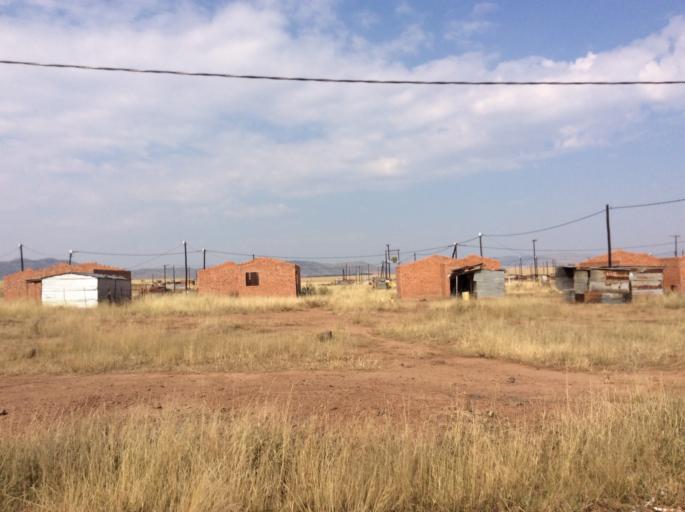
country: LS
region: Mafeteng
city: Mafeteng
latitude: -29.9892
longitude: 27.0047
